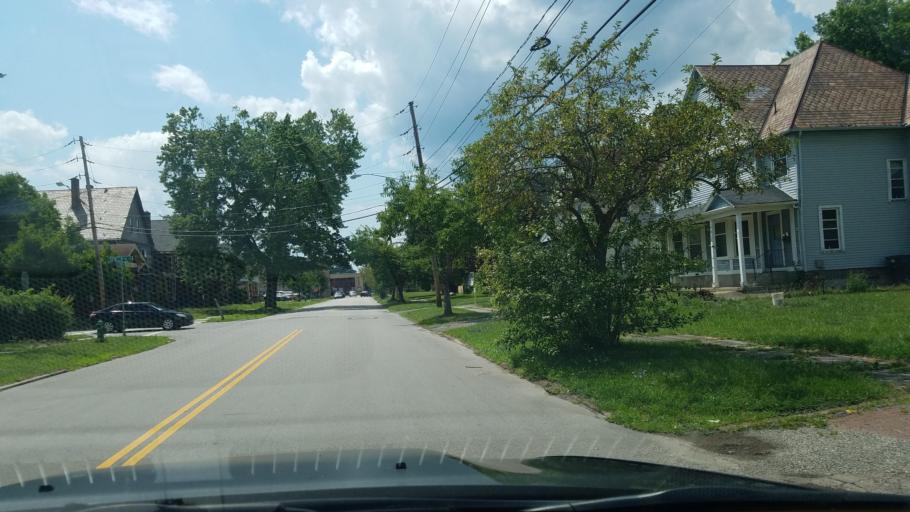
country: US
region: Ohio
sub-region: Trumbull County
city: Warren
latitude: 41.2391
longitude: -80.8149
